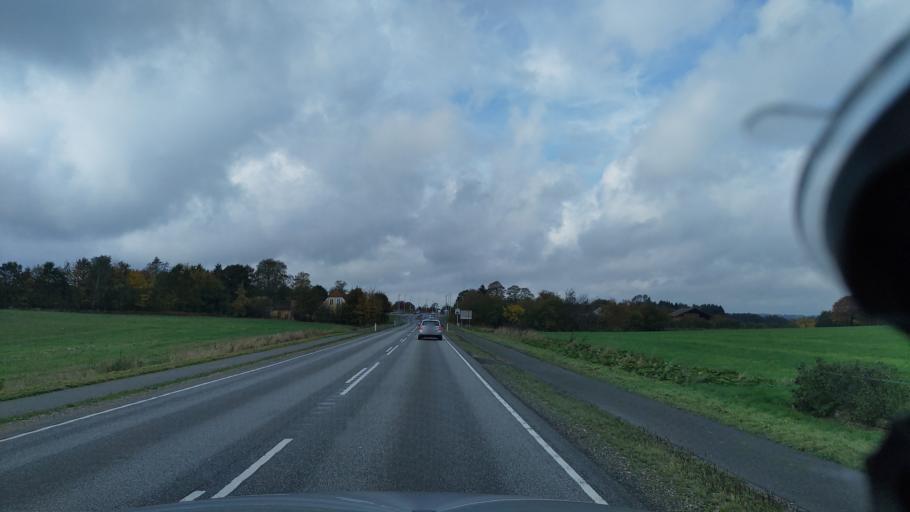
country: DK
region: Zealand
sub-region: Naestved Kommune
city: Fensmark
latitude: 55.2581
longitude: 11.8912
